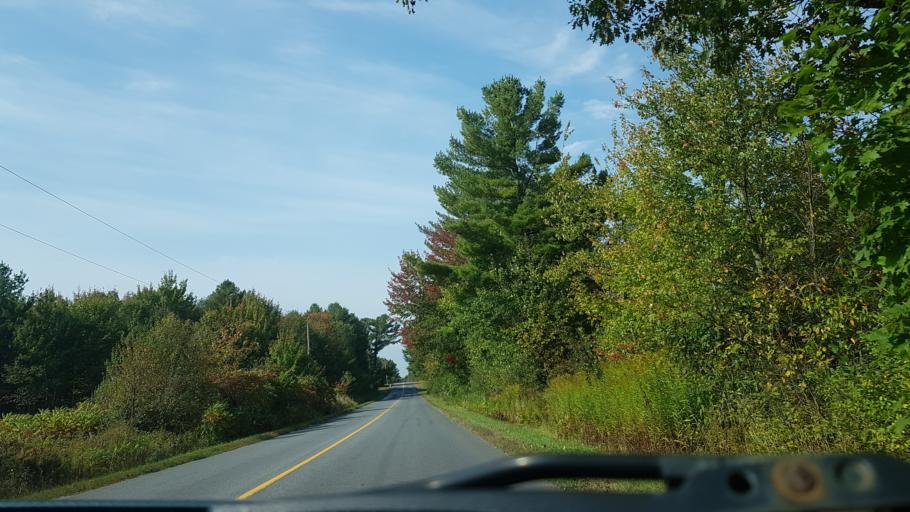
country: CA
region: Ontario
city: Gravenhurst
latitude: 44.7851
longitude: -79.2501
